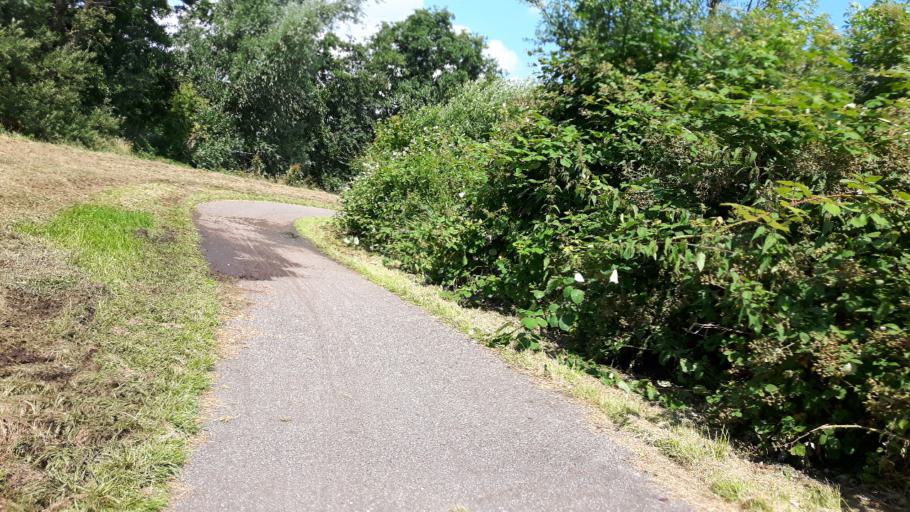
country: NL
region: South Holland
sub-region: Bodegraven-Reeuwijk
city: Reeuwijk
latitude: 52.0256
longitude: 4.7293
